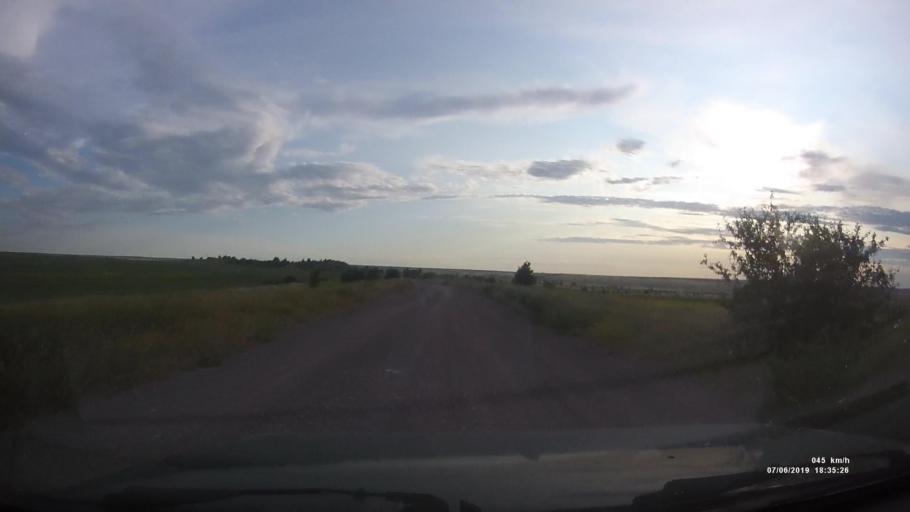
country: RU
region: Rostov
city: Staraya Stanitsa
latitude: 48.2552
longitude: 40.3590
